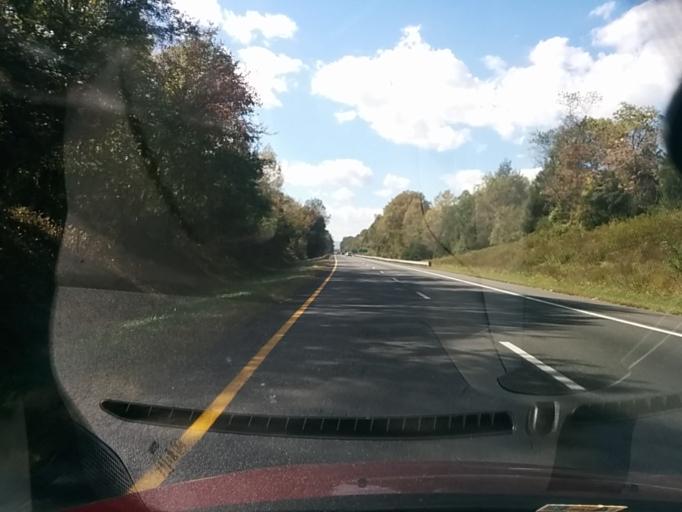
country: US
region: Virginia
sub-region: Albemarle County
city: Crozet
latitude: 38.0359
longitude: -78.6162
